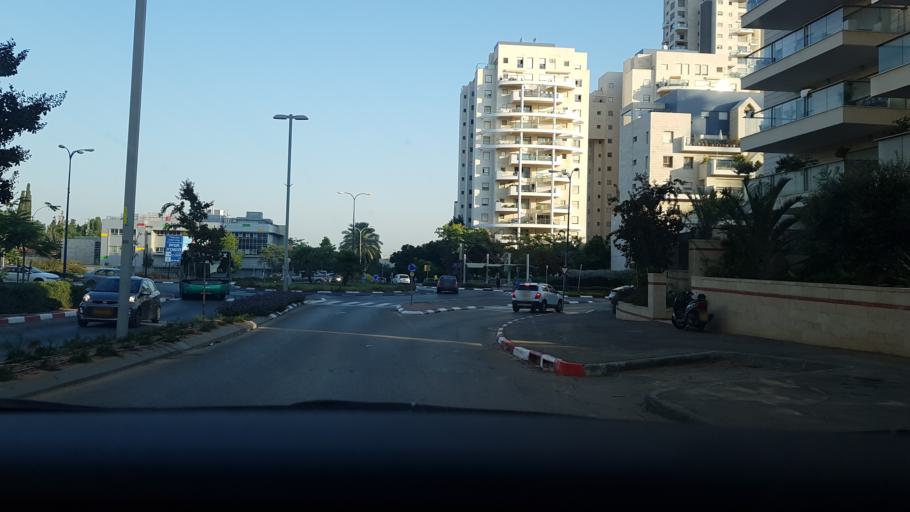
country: IL
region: Central District
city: Ness Ziona
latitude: 31.9048
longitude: 34.8211
